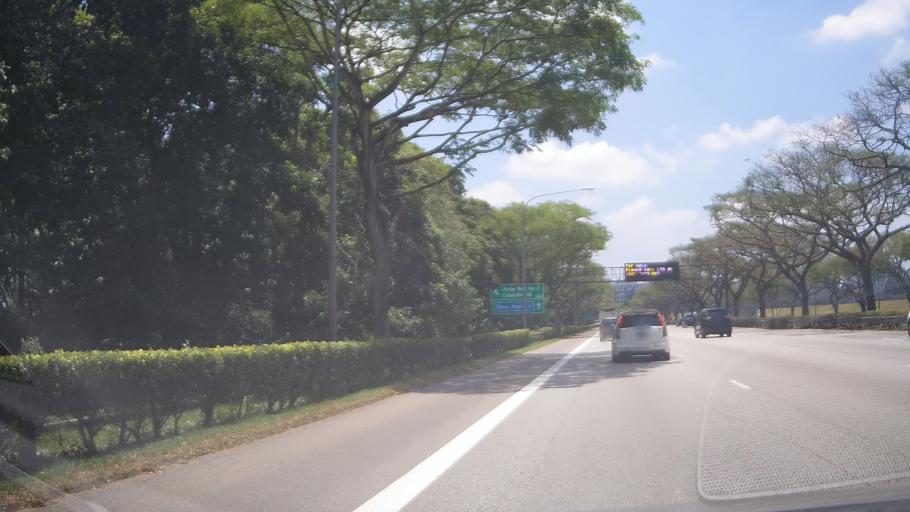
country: MY
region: Johor
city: Johor Bahru
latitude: 1.3600
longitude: 103.7114
